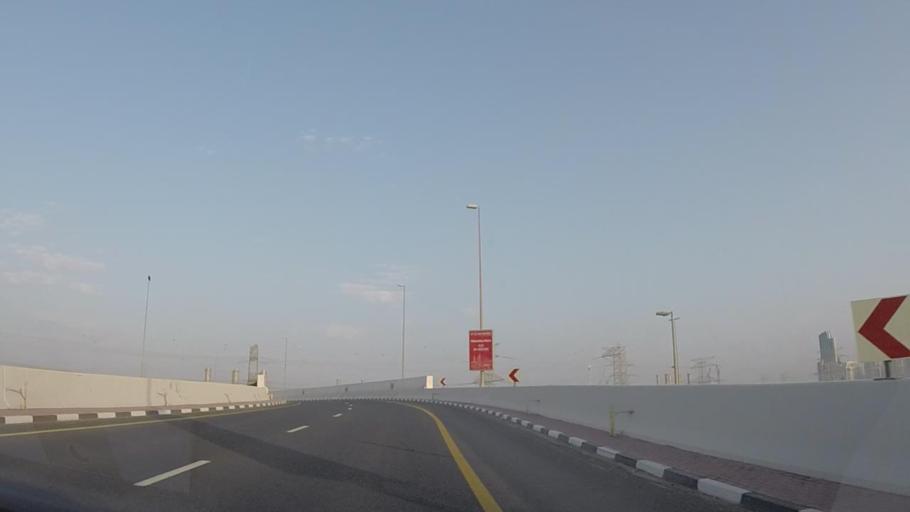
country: AE
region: Dubai
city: Dubai
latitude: 25.0517
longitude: 55.1207
